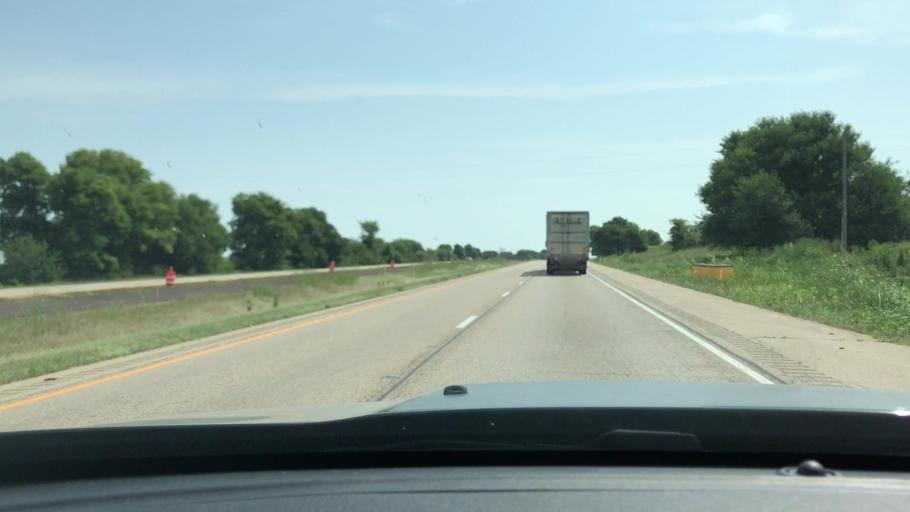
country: US
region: Illinois
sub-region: Bureau County
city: Walnut
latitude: 41.3874
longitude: -89.7430
